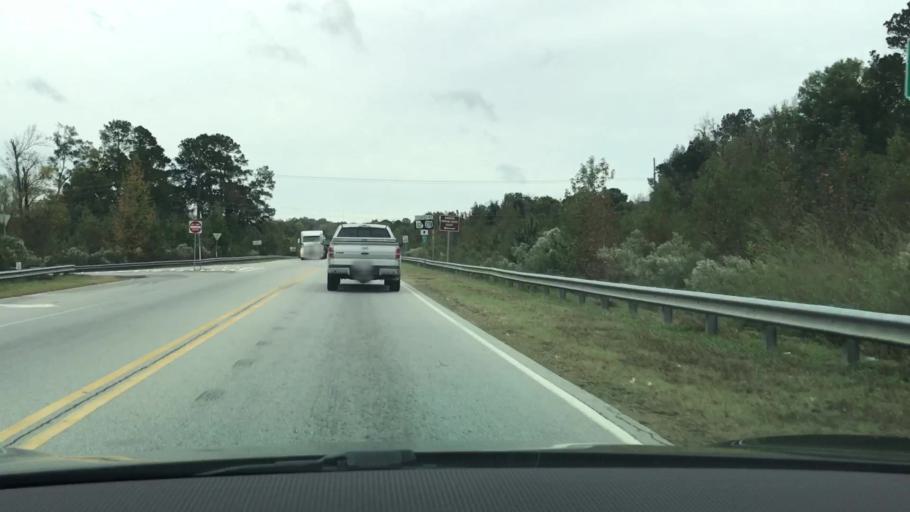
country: US
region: Georgia
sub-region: Warren County
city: West Warrenton
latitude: 33.4070
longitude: -82.6725
